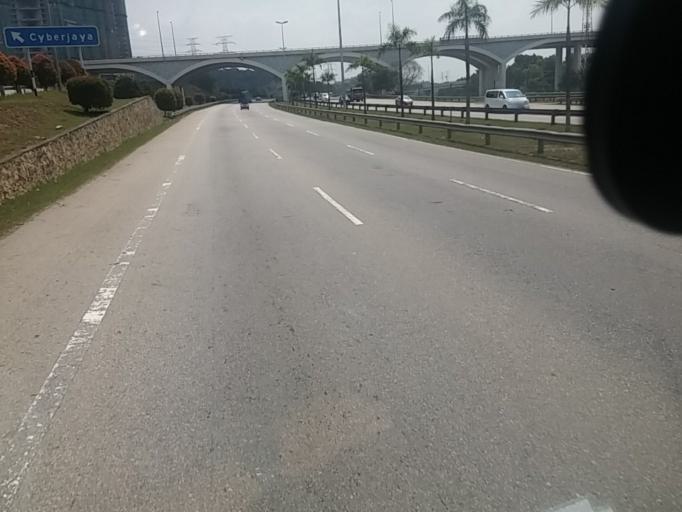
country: MY
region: Putrajaya
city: Putrajaya
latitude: 2.9568
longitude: 101.6580
